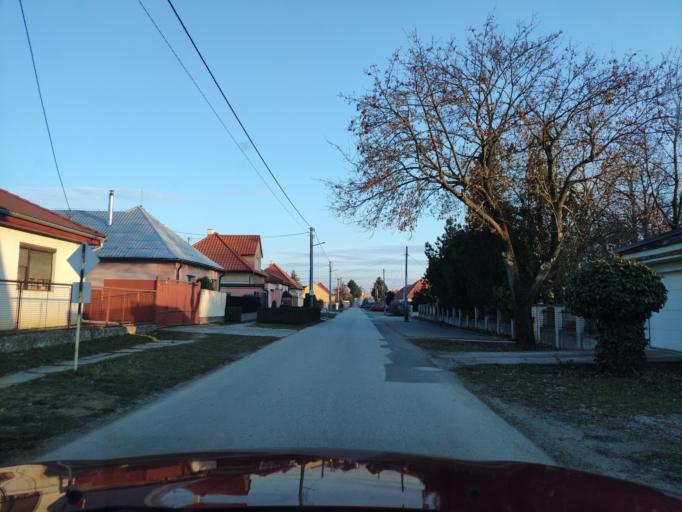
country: SK
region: Nitriansky
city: Sellye
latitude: 48.2335
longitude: 17.9323
